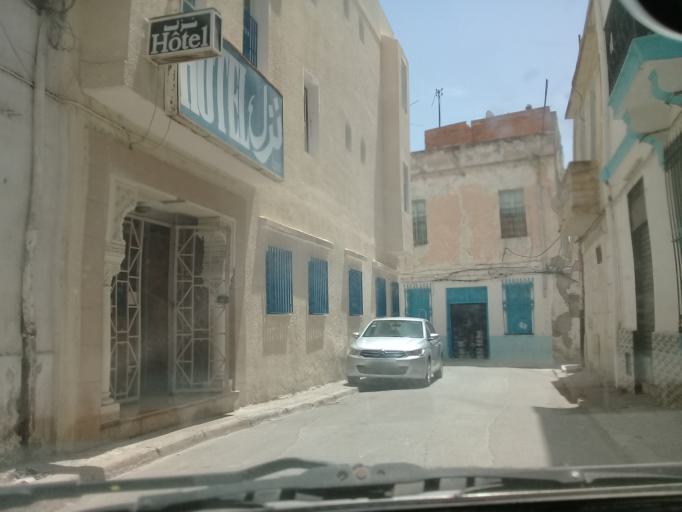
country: TN
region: Tunis
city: Tunis
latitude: 36.7928
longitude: 10.1777
